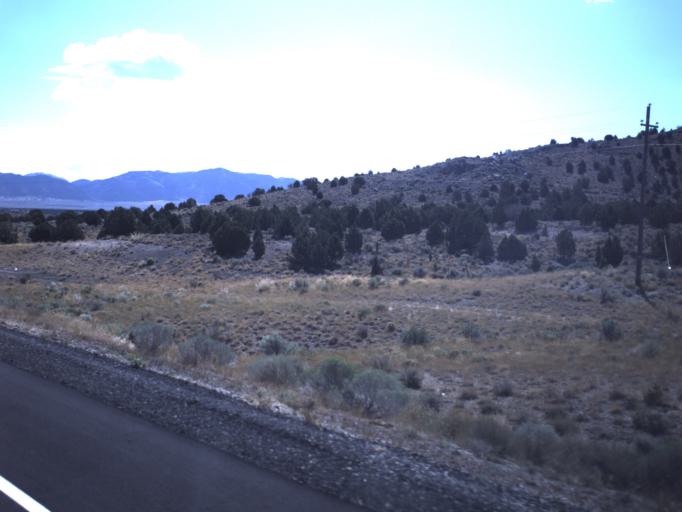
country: US
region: Utah
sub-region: Utah County
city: Eagle Mountain
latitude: 40.0720
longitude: -112.3680
